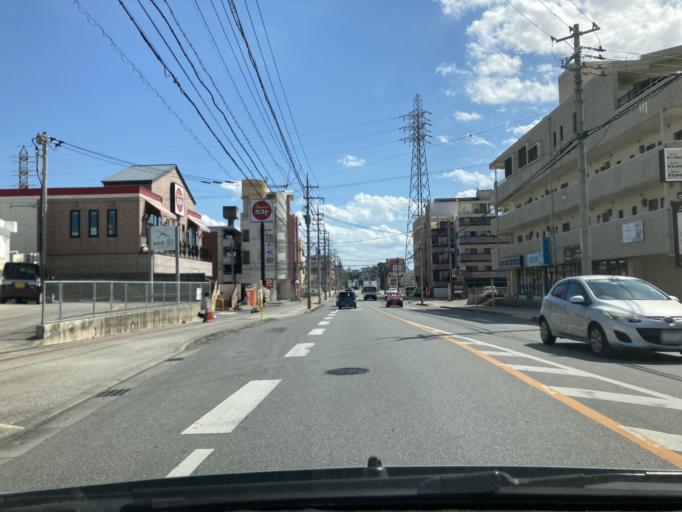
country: JP
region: Okinawa
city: Tomigusuku
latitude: 26.1900
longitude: 127.7087
